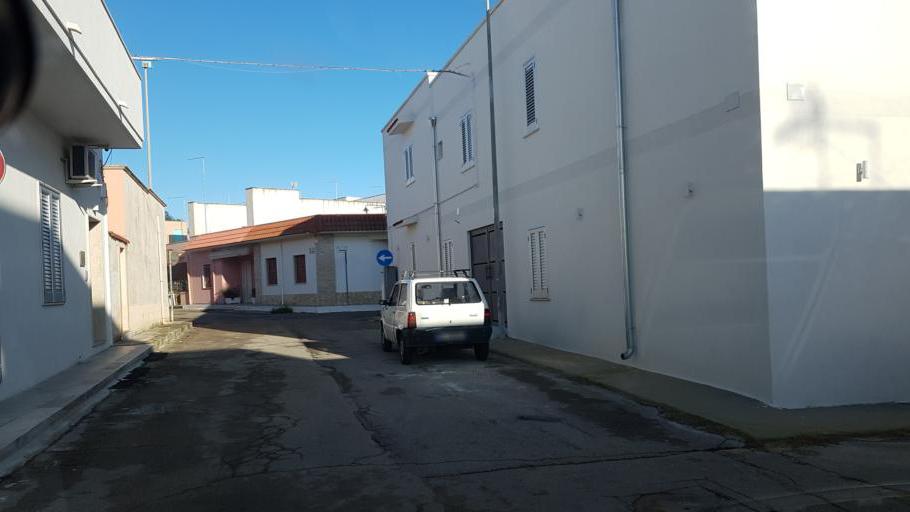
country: IT
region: Apulia
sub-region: Provincia di Brindisi
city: Torchiarolo
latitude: 40.5350
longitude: 18.0741
